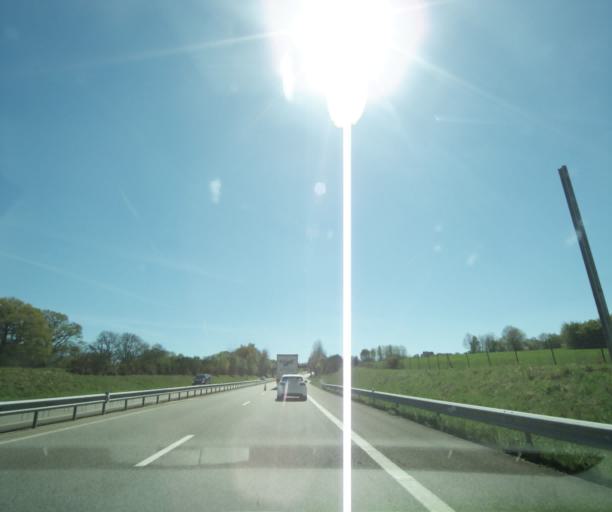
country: FR
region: Limousin
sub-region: Departement de la Haute-Vienne
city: Saint-Germain-les-Belles
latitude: 45.6131
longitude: 1.4492
